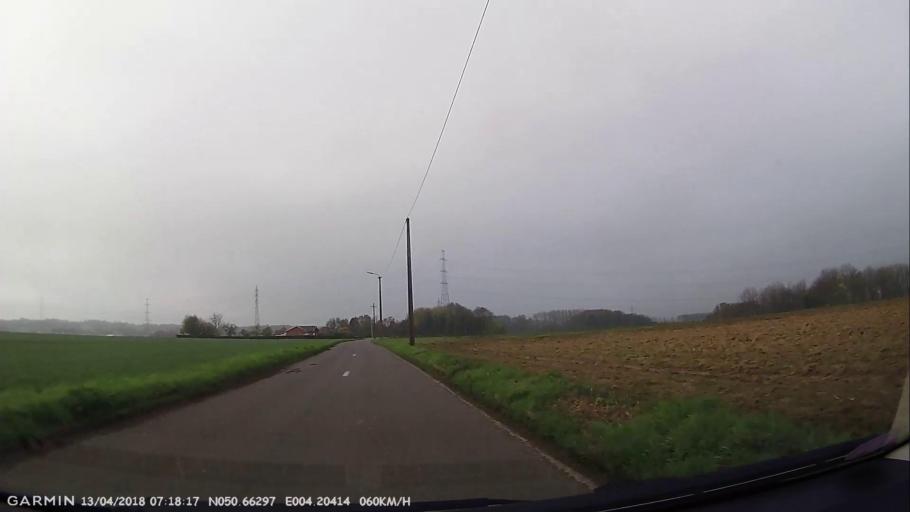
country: BE
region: Wallonia
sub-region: Province du Brabant Wallon
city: Tubize
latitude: 50.6627
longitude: 4.2040
